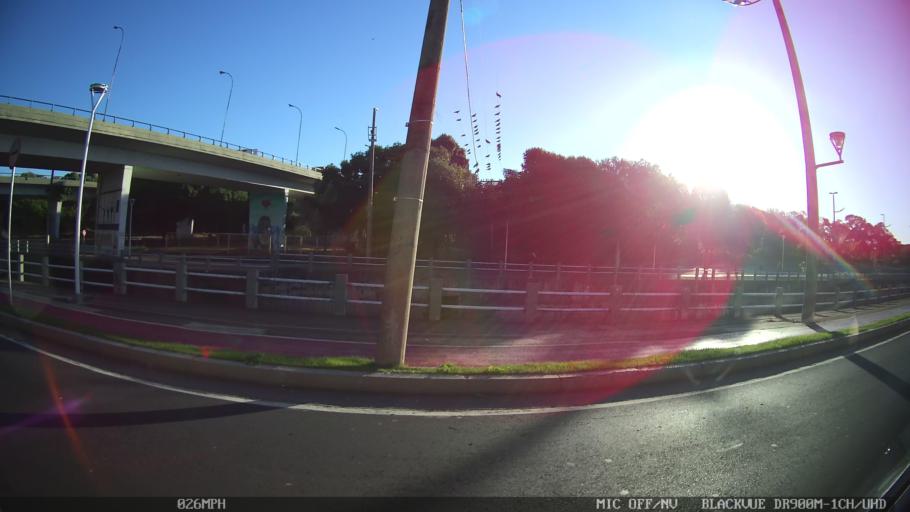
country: BR
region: Sao Paulo
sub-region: Sao Jose Do Rio Preto
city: Sao Jose do Rio Preto
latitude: -20.8027
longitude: -49.3776
